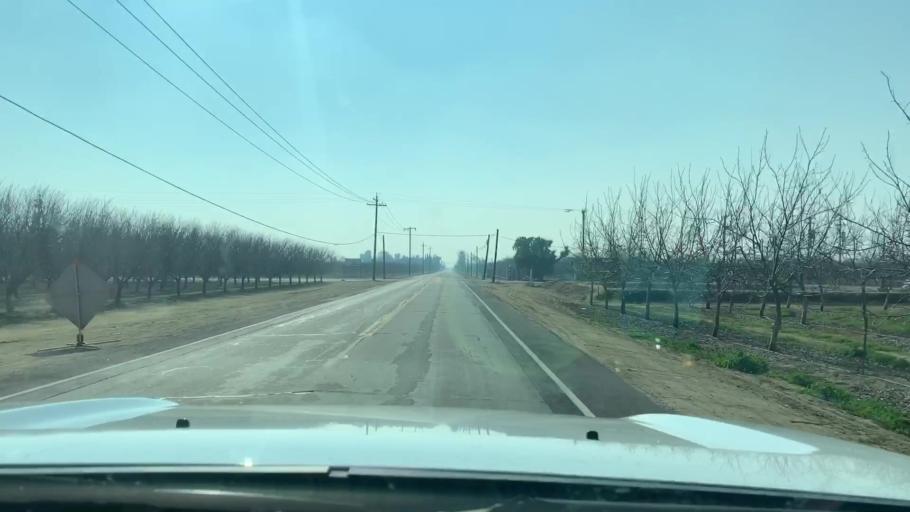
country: US
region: California
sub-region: Kern County
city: Shafter
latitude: 35.4863
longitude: -119.2785
